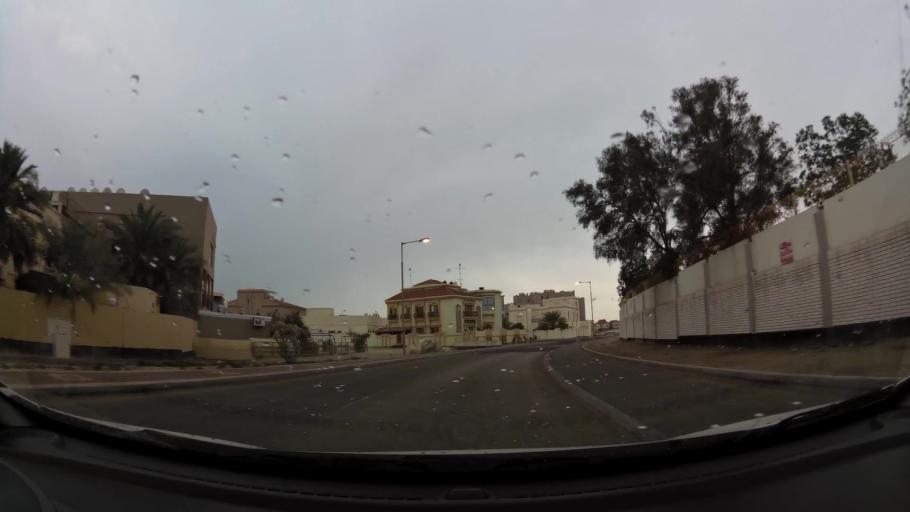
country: BH
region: Central Governorate
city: Madinat Hamad
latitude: 26.1314
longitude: 50.4951
